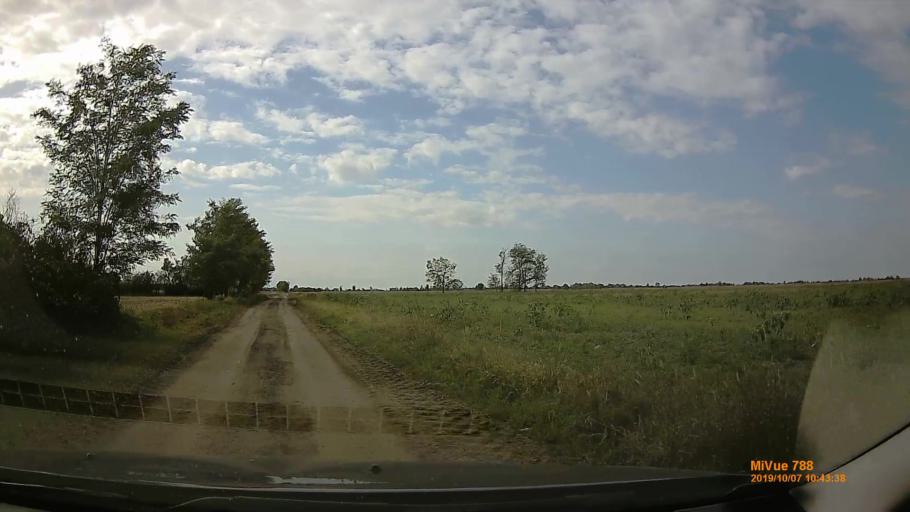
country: HU
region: Bekes
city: Kondoros
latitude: 46.7357
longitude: 20.8351
